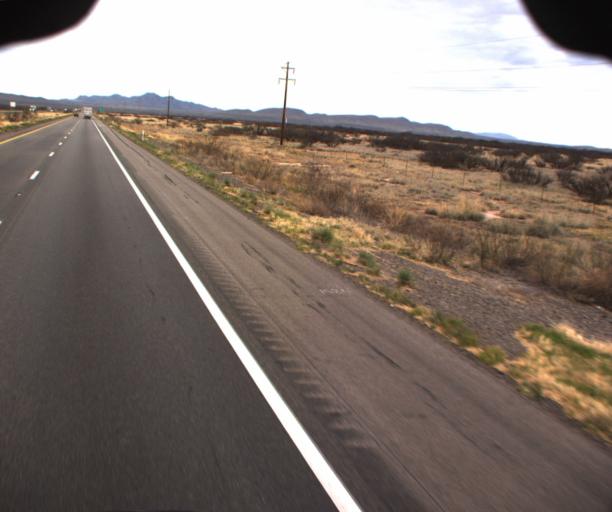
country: US
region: Arizona
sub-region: Cochise County
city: Willcox
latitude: 32.2005
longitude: -109.9094
